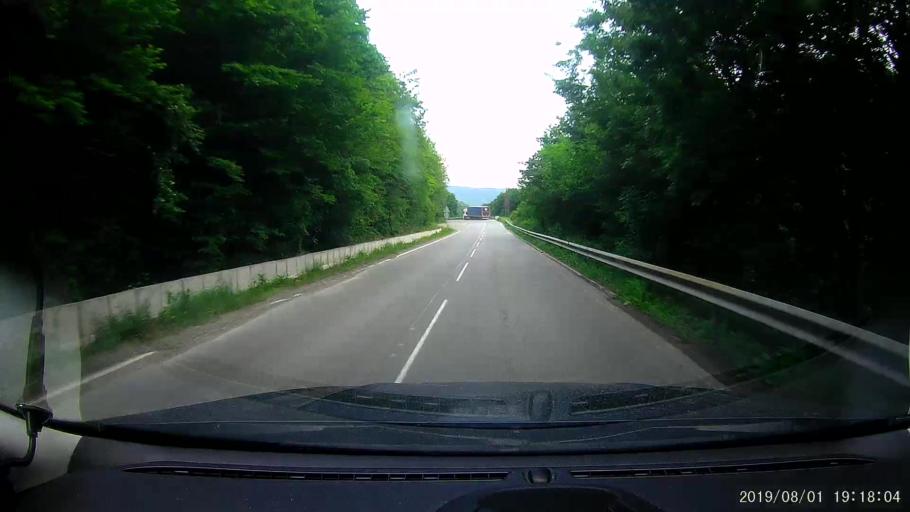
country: BG
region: Shumen
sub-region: Obshtina Smyadovo
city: Smyadovo
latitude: 42.9174
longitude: 26.9384
